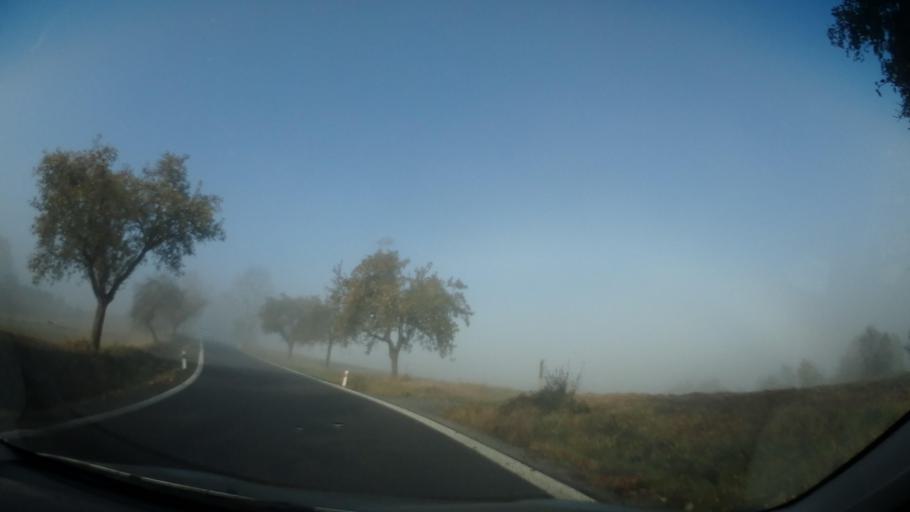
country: CZ
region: Vysocina
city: Krizanov
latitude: 49.4410
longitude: 16.1842
